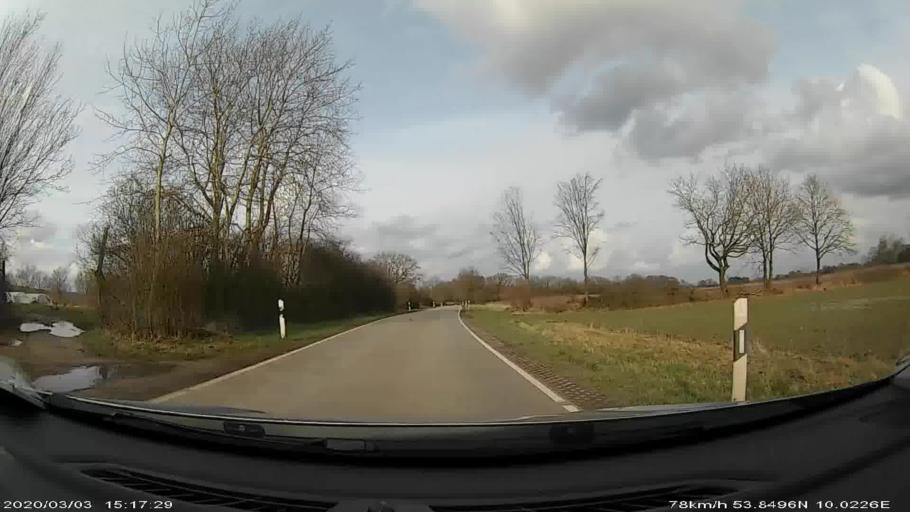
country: DE
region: Schleswig-Holstein
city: Kattendorf
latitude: 53.8491
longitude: 10.0226
